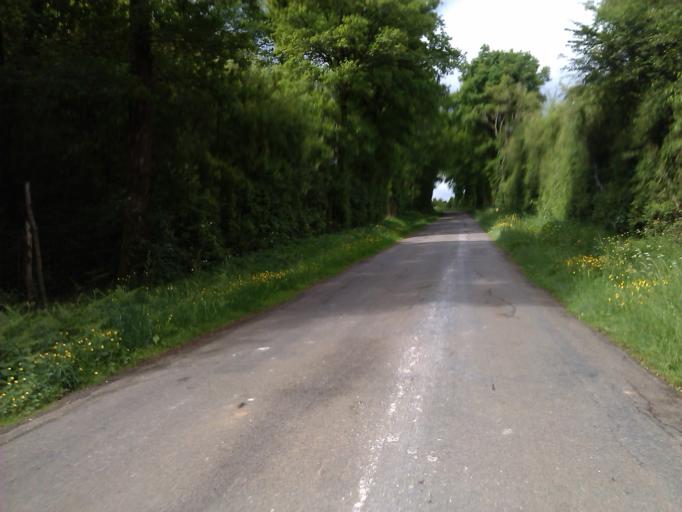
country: FR
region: Poitou-Charentes
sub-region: Departement de la Vienne
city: Charroux
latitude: 46.1035
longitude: 0.5263
